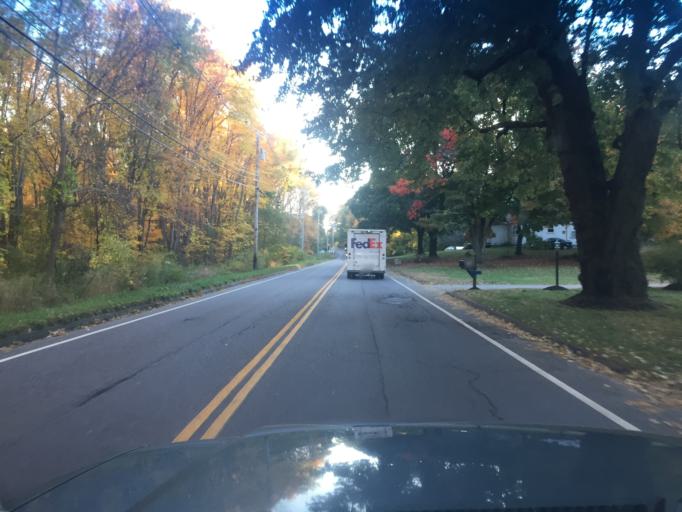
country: US
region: Massachusetts
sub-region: Middlesex County
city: Hudson
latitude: 42.3928
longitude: -71.5402
